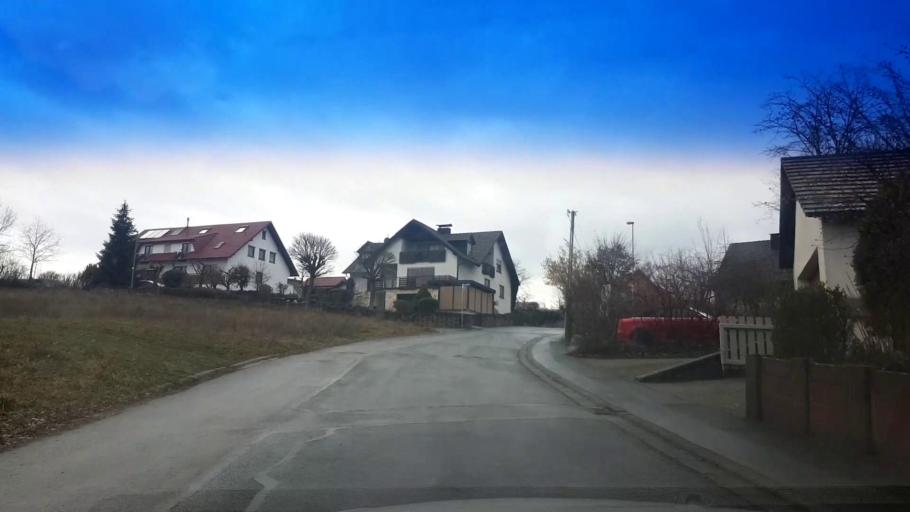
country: DE
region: Bavaria
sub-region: Upper Franconia
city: Litzendorf
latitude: 49.8697
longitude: 11.0237
